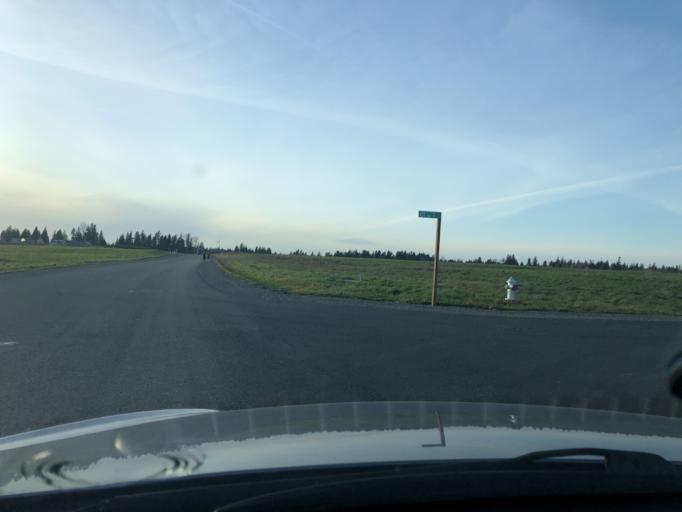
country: US
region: Washington
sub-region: Pierce County
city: Prairie Ridge
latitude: 47.1939
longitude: -122.1148
